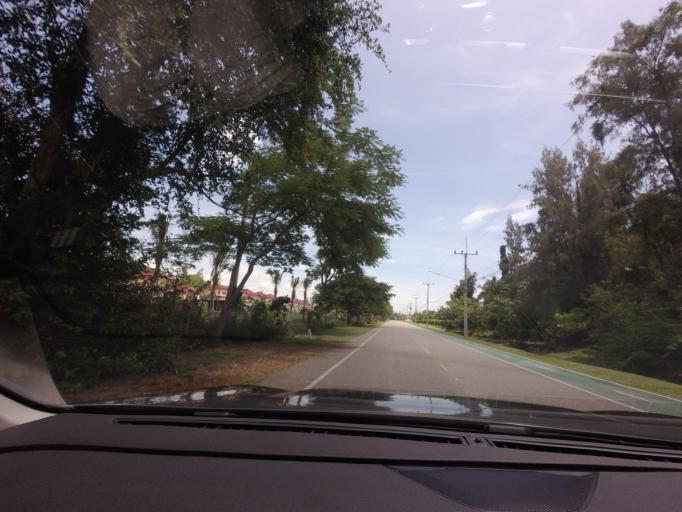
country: TH
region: Prachuap Khiri Khan
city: Hua Hin
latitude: 12.5008
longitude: 99.9727
